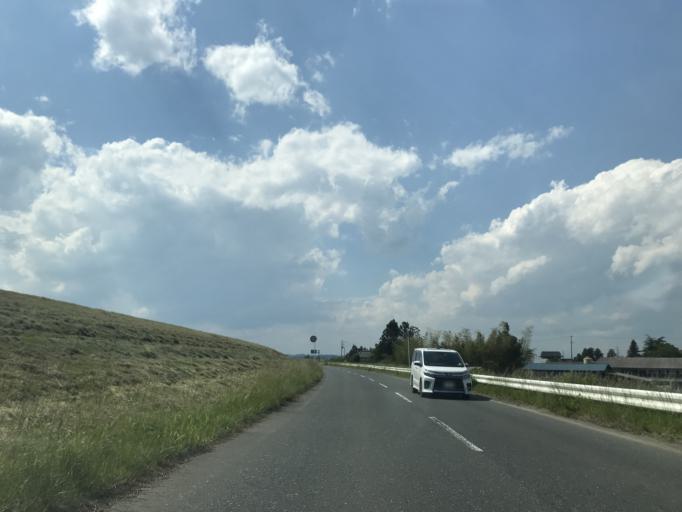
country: JP
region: Miyagi
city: Matsushima
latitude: 38.4436
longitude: 141.1143
